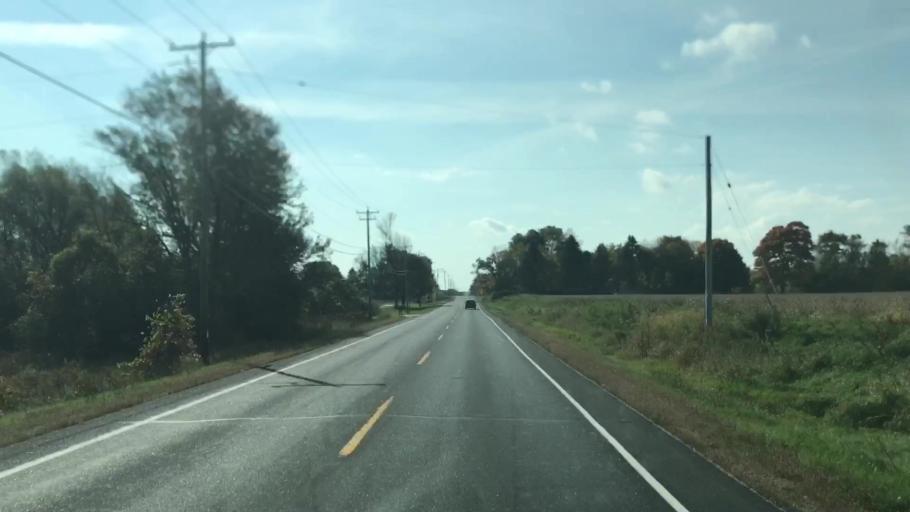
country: US
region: Wisconsin
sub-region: Ozaukee County
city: Mequon
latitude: 43.2161
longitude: -88.0435
